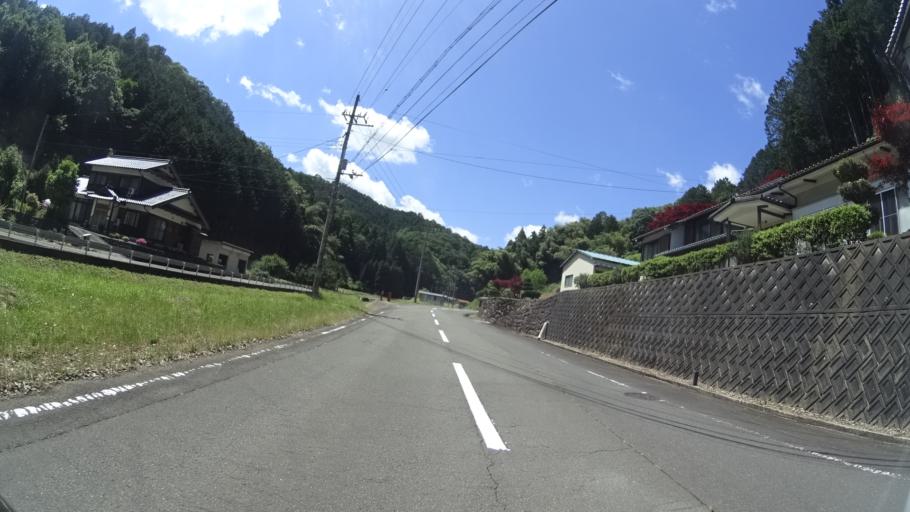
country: JP
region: Kyoto
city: Miyazu
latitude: 35.4147
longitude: 135.1879
